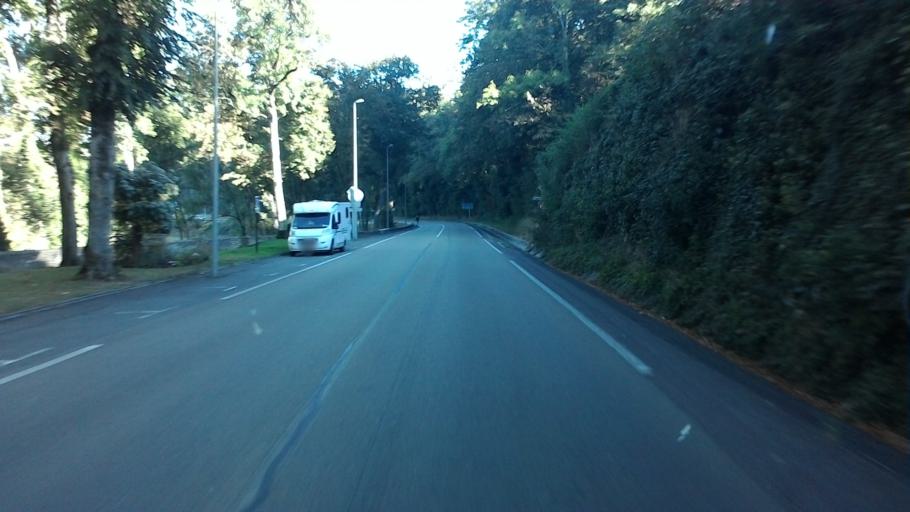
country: FR
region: Champagne-Ardenne
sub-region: Departement de la Haute-Marne
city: Chaumont
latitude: 48.1110
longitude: 5.1233
